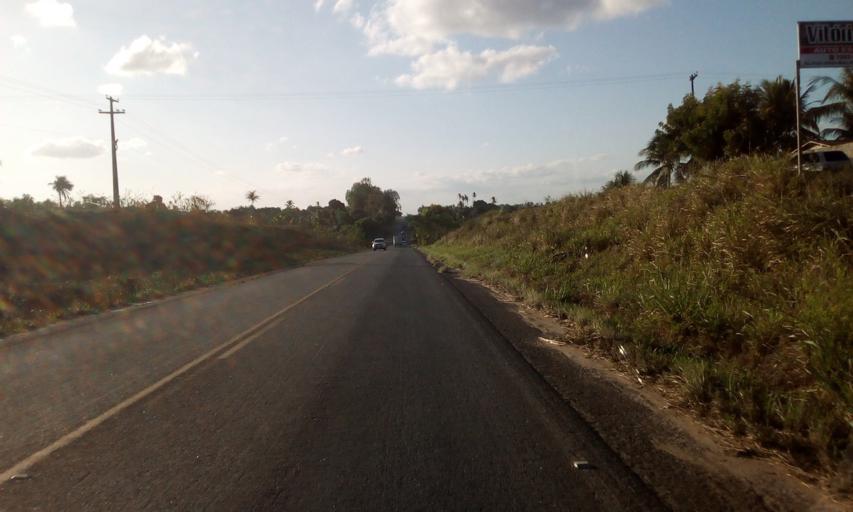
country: BR
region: Paraiba
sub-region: Mari
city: Mari
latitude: -7.0777
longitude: -35.2584
